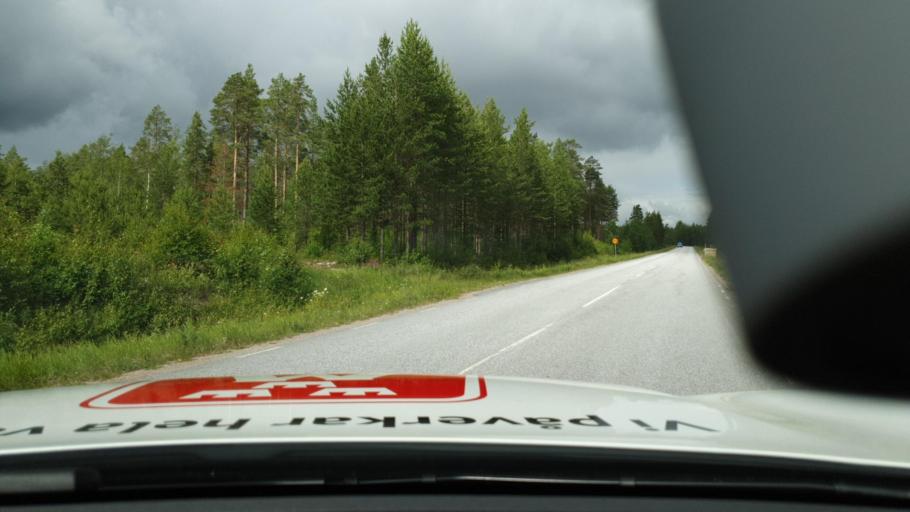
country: SE
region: Norrbotten
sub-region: Lulea Kommun
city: Sodra Sunderbyn
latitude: 65.4849
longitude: 21.9014
